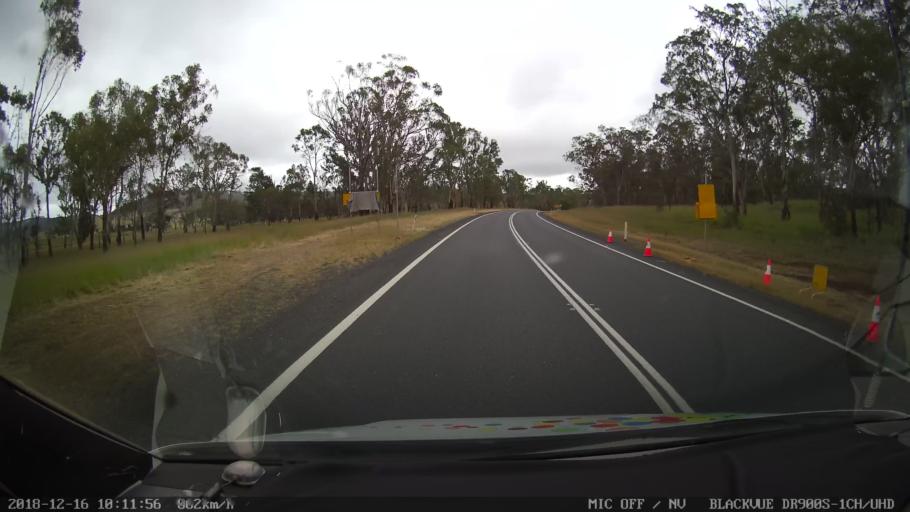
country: AU
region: New South Wales
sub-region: Glen Innes Severn
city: Glen Innes
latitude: -29.3094
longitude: 151.9357
